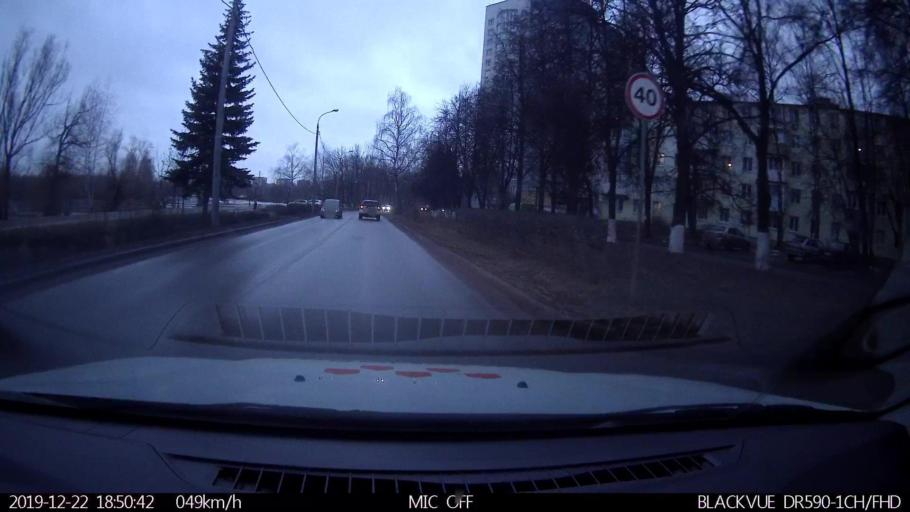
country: RU
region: Nizjnij Novgorod
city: Gorbatovka
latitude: 56.3418
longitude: 43.8481
